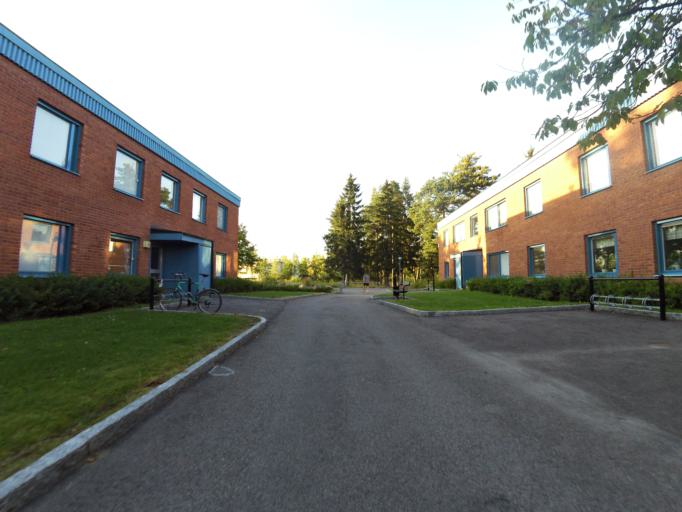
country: SE
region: Gaevleborg
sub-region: Gavle Kommun
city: Gavle
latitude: 60.6550
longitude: 17.1341
